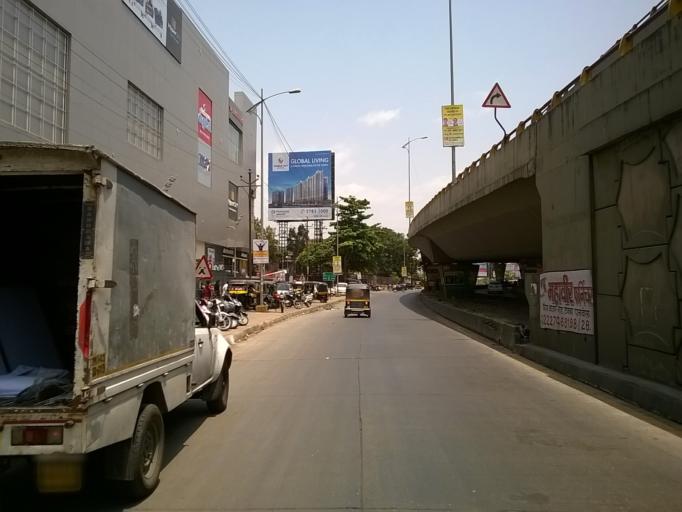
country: IN
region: Maharashtra
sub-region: Raigarh
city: Panvel
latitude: 18.9933
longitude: 73.1153
